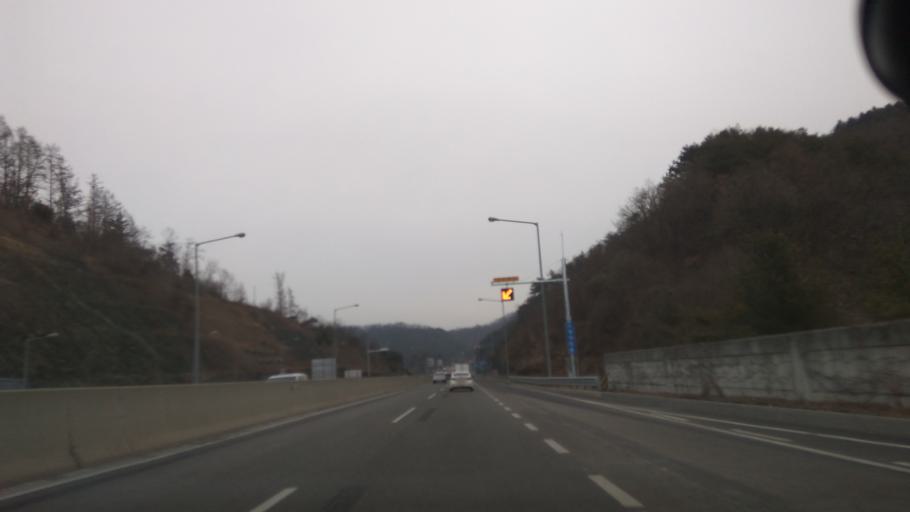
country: KR
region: Gangwon-do
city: Sindong
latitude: 37.7354
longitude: 127.6266
